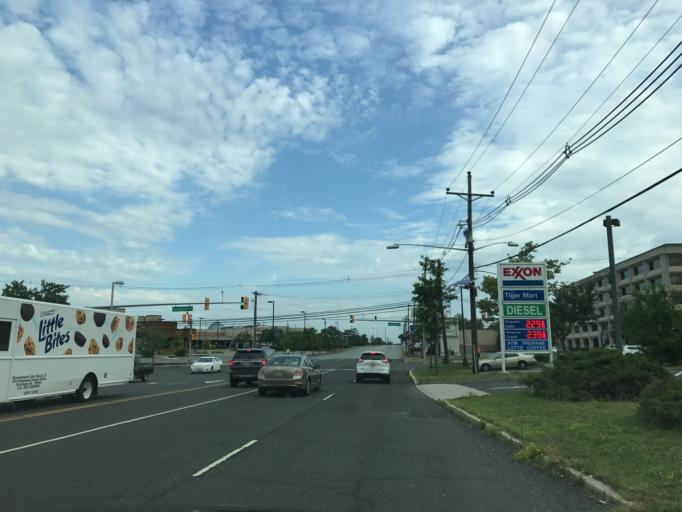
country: US
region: New Jersey
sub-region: Middlesex County
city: Fords
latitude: 40.5451
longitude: -74.3310
